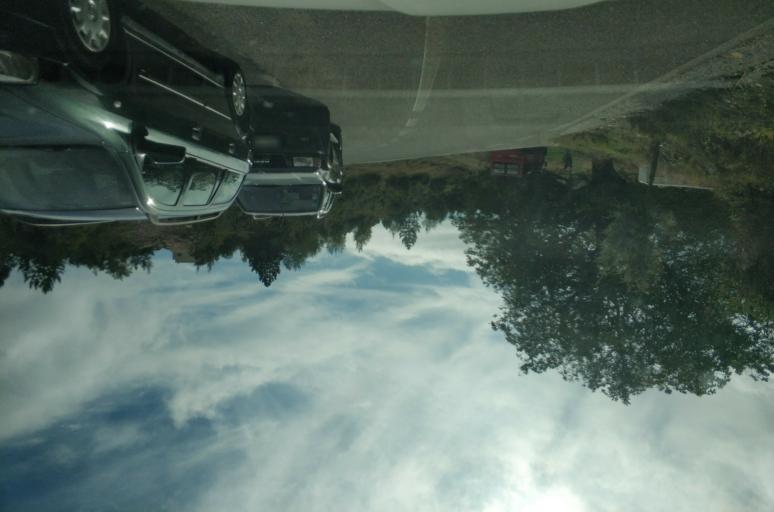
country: AL
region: Durres
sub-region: Rrethi i Krujes
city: Kruje
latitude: 41.5182
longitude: 19.8036
